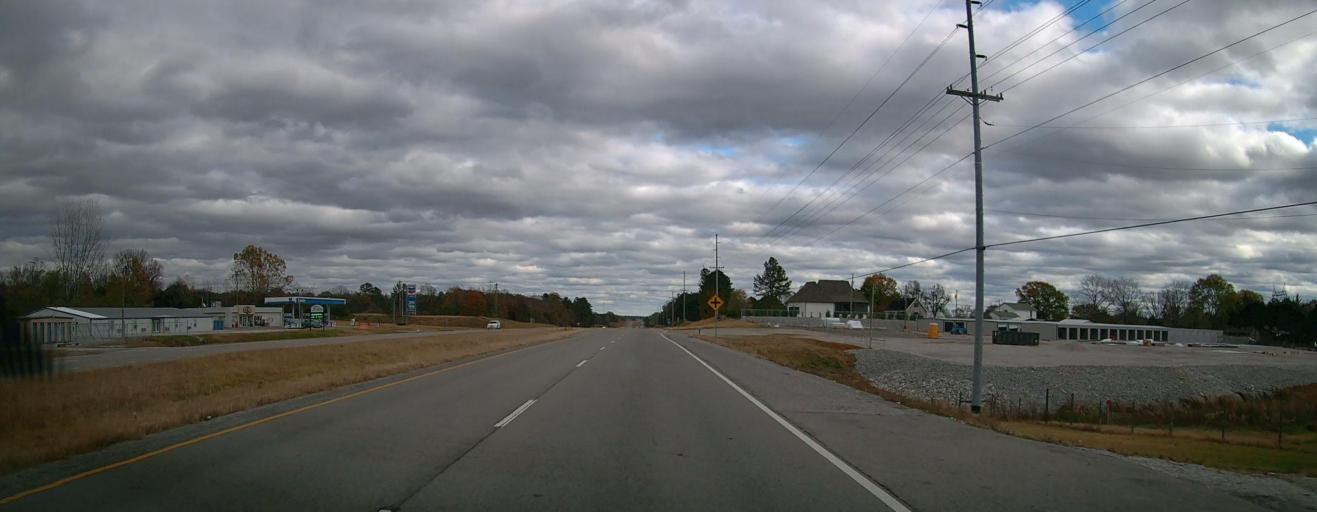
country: US
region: Alabama
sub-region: Lawrence County
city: Moulton
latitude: 34.5676
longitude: -87.3736
